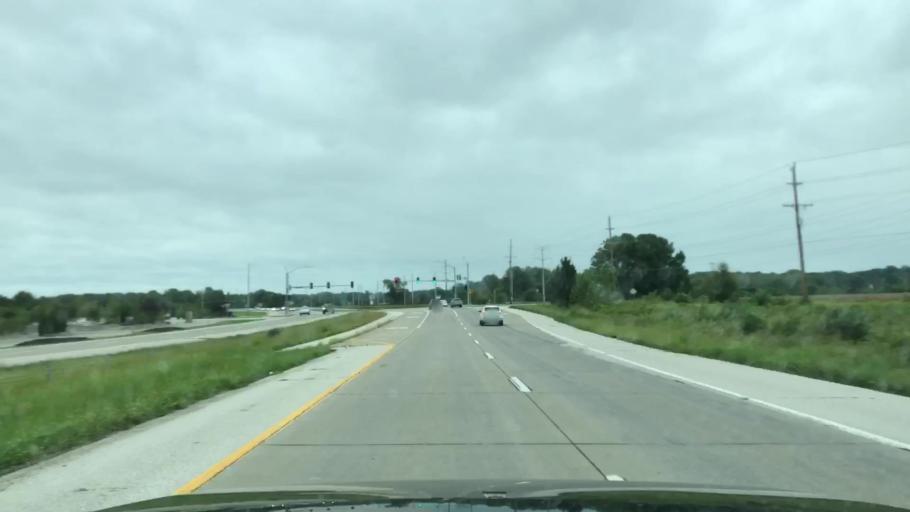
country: US
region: Missouri
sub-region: Saint Charles County
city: Saint Charles
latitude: 38.7296
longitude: -90.4891
